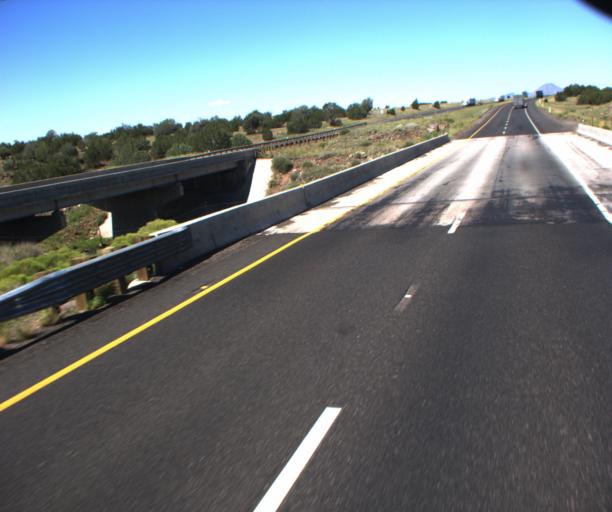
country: US
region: Arizona
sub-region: Yavapai County
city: Paulden
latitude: 35.2212
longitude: -112.5390
